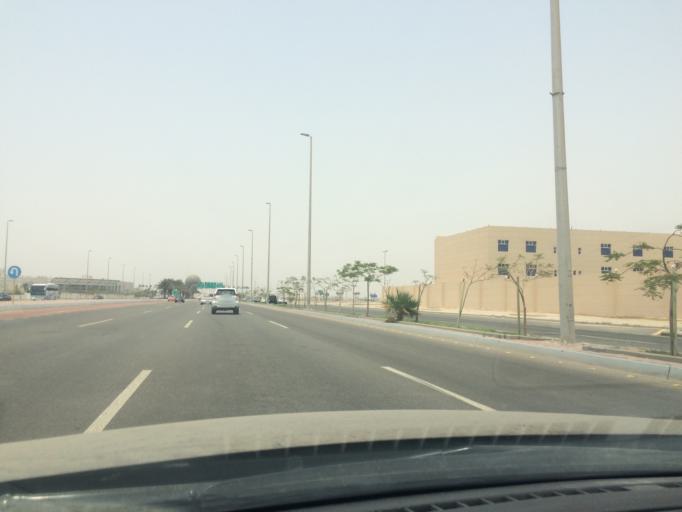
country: SA
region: Makkah
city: Jeddah
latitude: 21.6594
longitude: 39.1111
